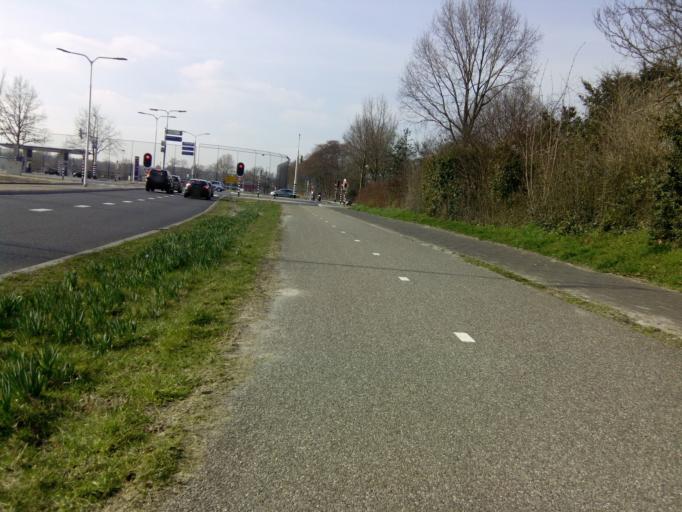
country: NL
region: Utrecht
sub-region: Gemeente Leusden
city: Leusden
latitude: 52.1245
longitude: 5.4140
